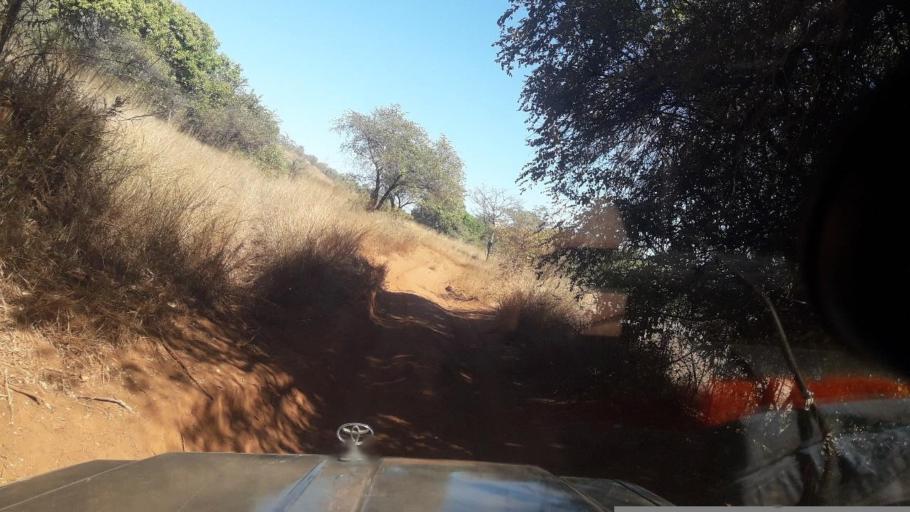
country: MG
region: Boeny
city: Sitampiky
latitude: -16.3133
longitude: 45.6301
